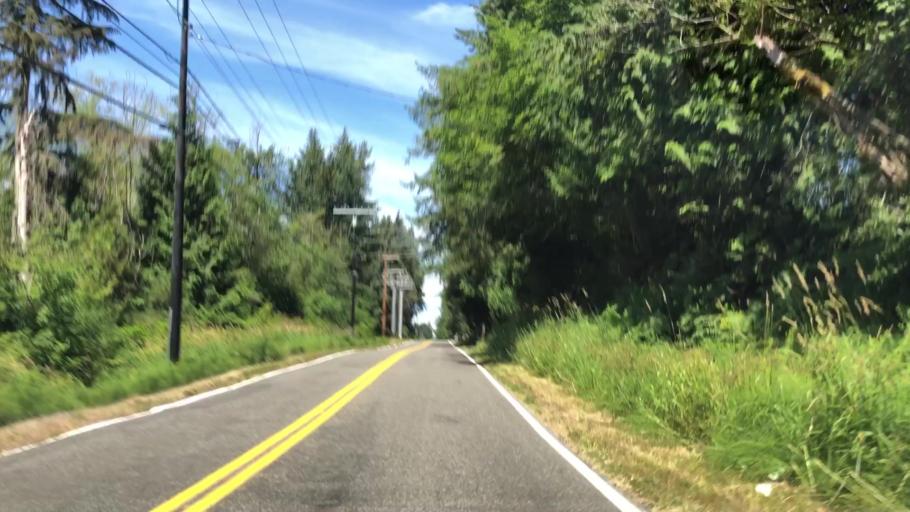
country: US
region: Washington
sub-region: Snohomish County
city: North Creek
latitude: 47.8290
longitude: -122.1642
